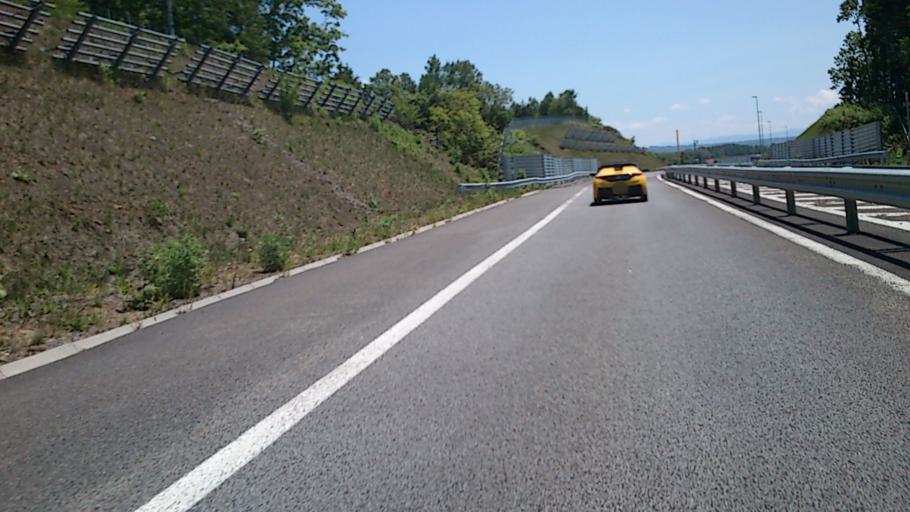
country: JP
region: Hokkaido
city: Nayoro
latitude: 44.4839
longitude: 142.3645
